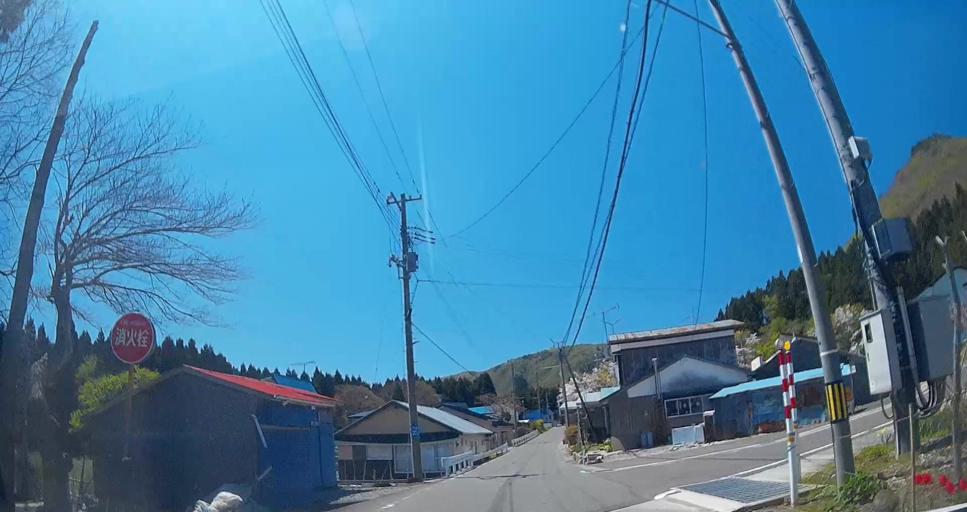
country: JP
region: Aomori
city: Mutsu
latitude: 41.3705
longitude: 141.4462
